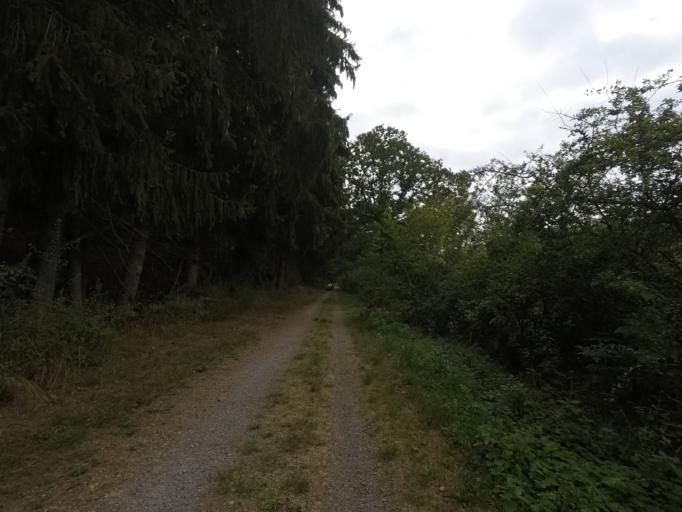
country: BE
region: Wallonia
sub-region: Province du Luxembourg
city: Martelange
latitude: 49.8457
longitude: 5.7130
